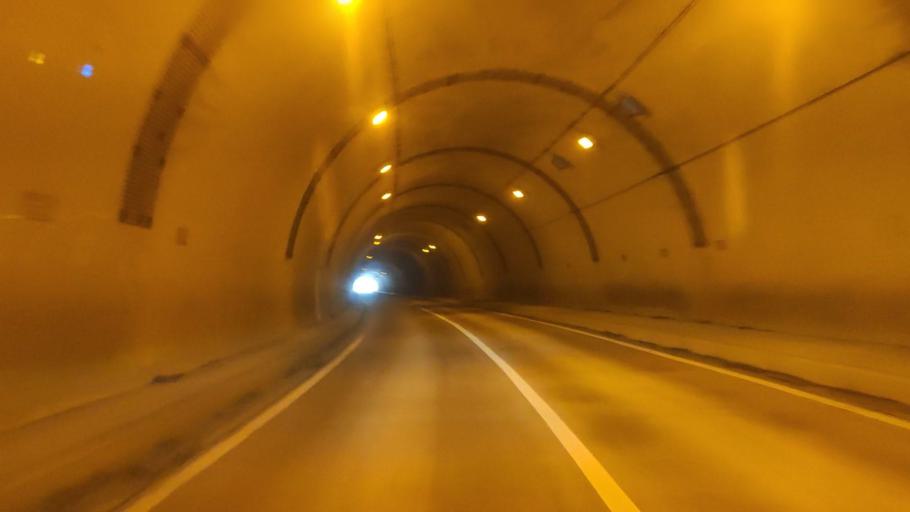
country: JP
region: Kumamoto
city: Hitoyoshi
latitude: 32.3827
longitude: 130.8352
